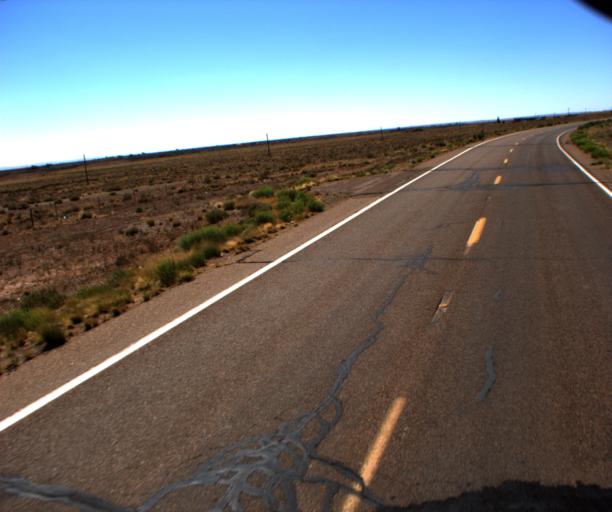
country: US
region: Arizona
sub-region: Coconino County
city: LeChee
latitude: 35.2899
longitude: -110.9858
